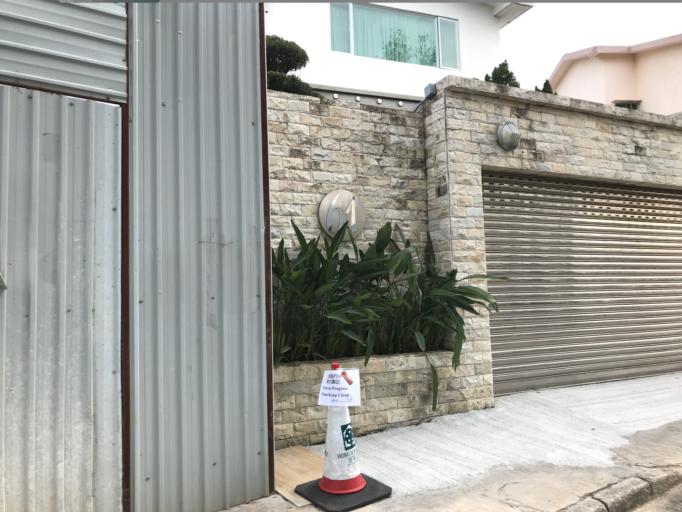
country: HK
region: Tai Po
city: Tai Po
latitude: 22.4613
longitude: 114.1553
